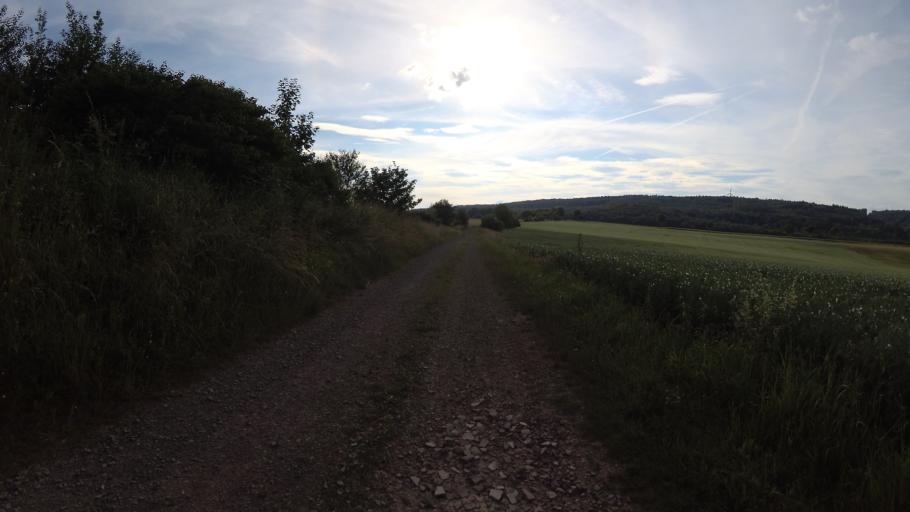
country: DE
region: Rheinland-Pfalz
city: Altenkirchen
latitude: 49.4578
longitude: 7.3166
